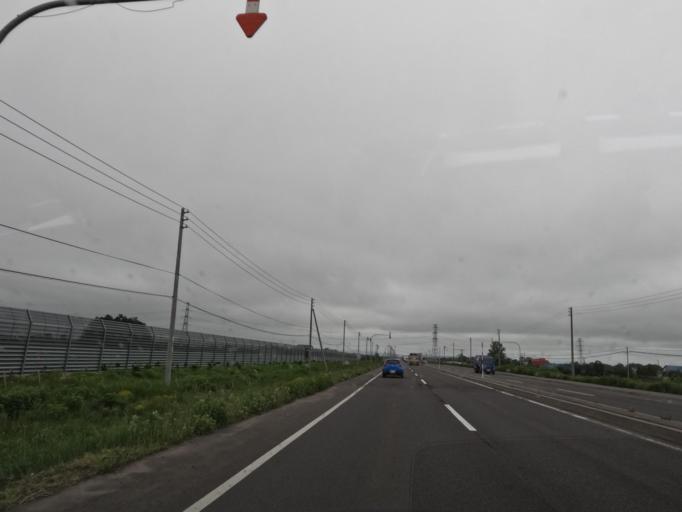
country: JP
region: Hokkaido
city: Ebetsu
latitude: 43.1565
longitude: 141.5187
